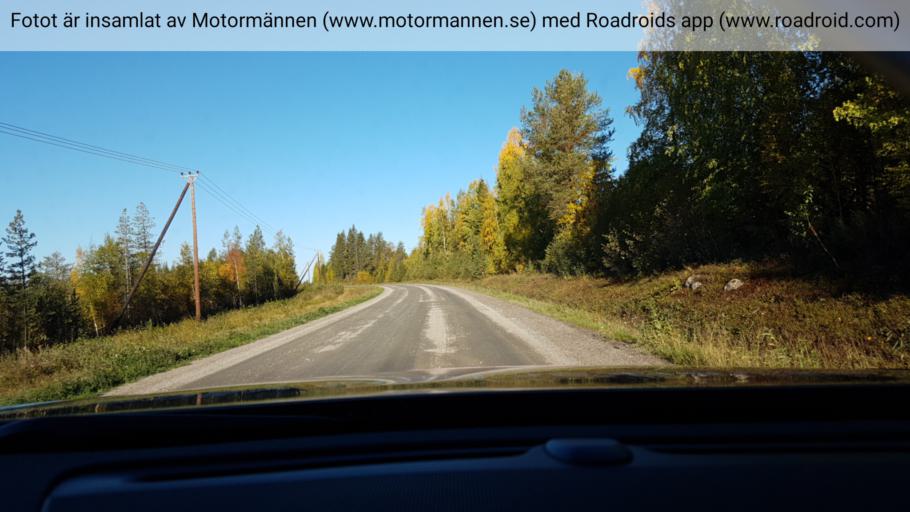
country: SE
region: Norrbotten
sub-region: Alvsbyns Kommun
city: AElvsbyn
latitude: 66.1794
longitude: 21.2302
